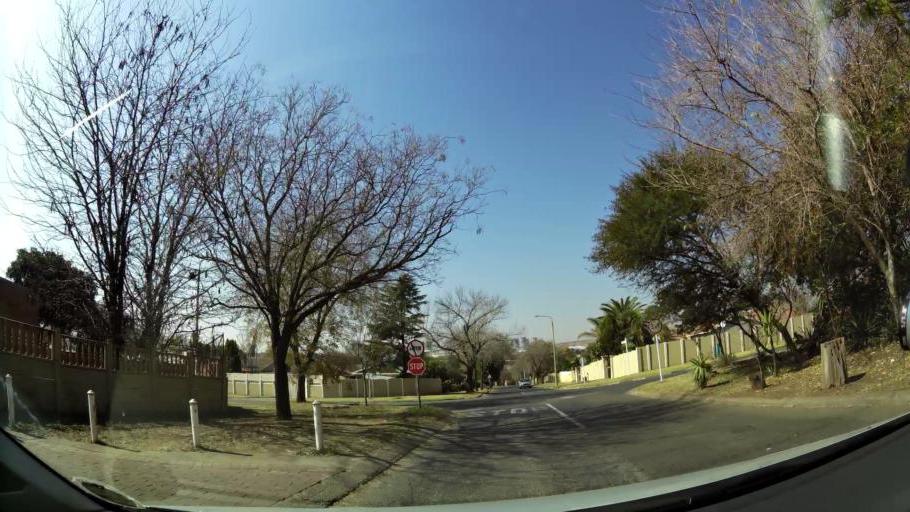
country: ZA
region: Gauteng
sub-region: City of Johannesburg Metropolitan Municipality
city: Modderfontein
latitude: -26.1138
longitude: 28.1655
